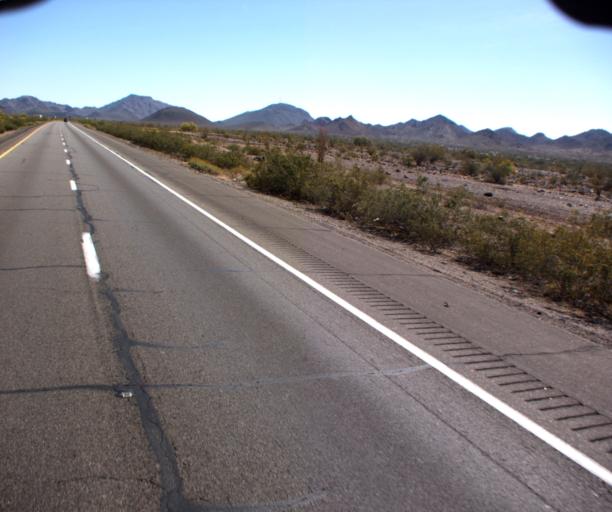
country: US
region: Arizona
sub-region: La Paz County
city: Quartzsite
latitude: 33.6757
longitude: -114.1269
